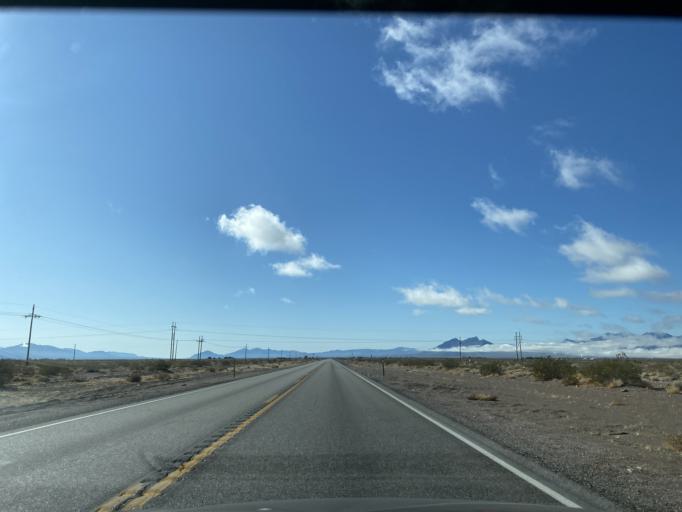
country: US
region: Nevada
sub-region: Nye County
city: Beatty
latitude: 36.5424
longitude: -116.4175
